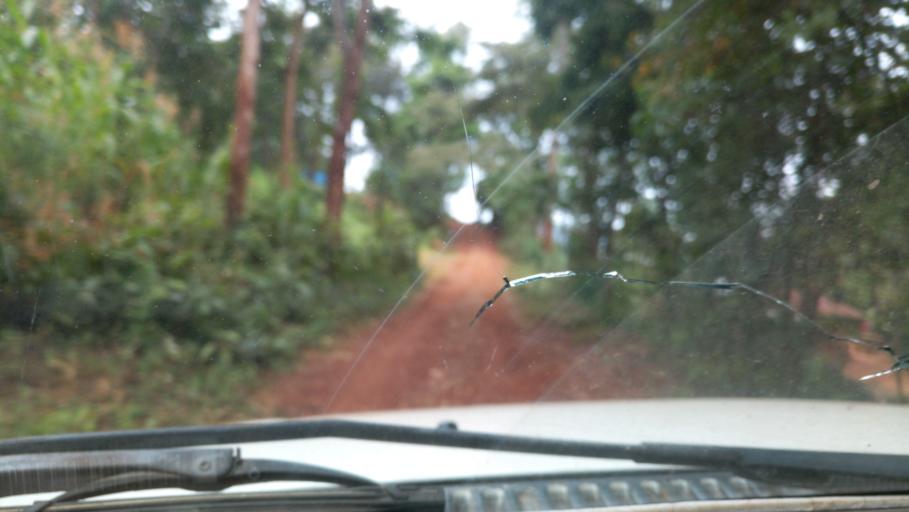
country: KE
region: Murang'a District
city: Murang'a
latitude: -0.7125
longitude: 37.1045
